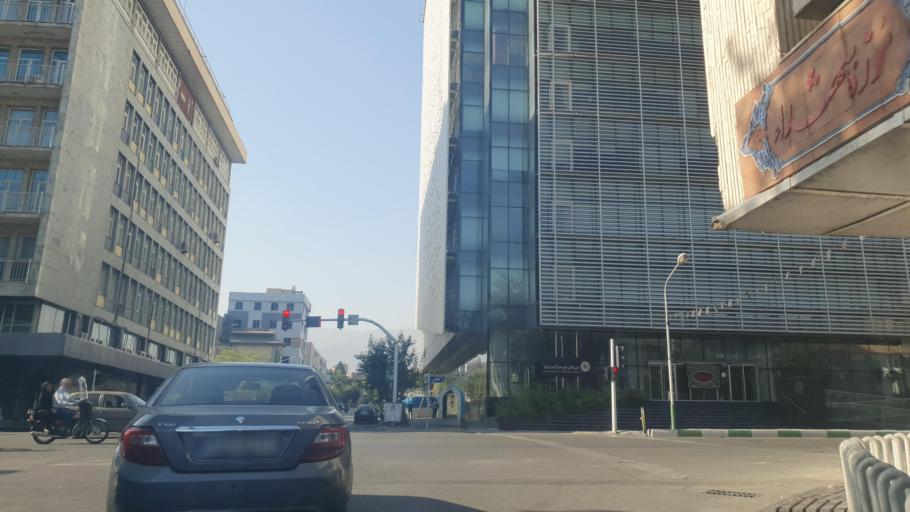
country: IR
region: Tehran
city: Tehran
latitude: 35.7066
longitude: 51.4211
